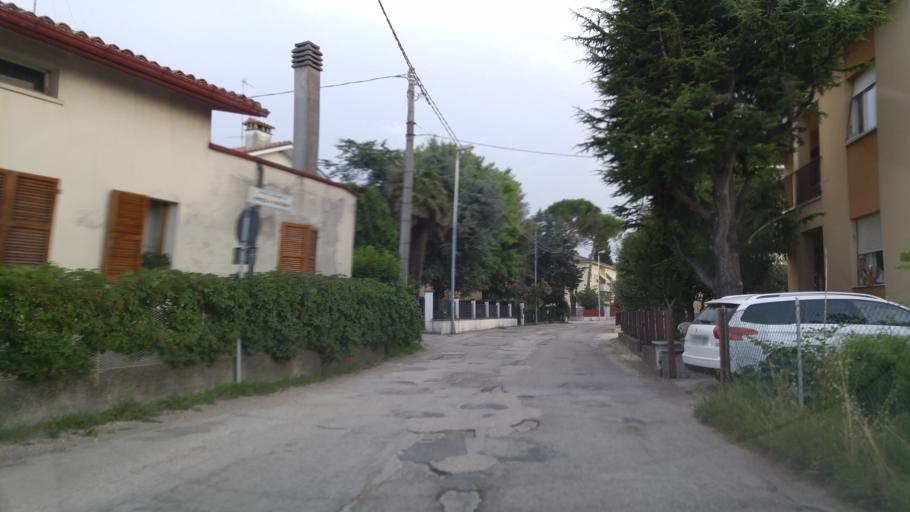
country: IT
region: The Marches
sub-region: Provincia di Pesaro e Urbino
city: Rosciano
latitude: 43.8216
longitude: 12.9962
